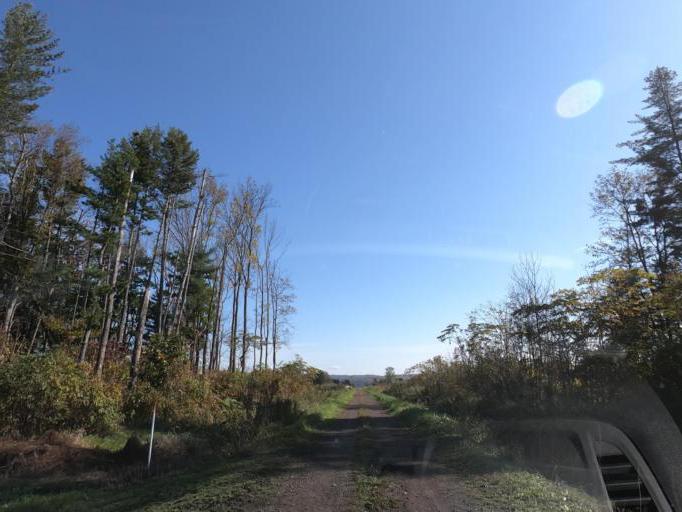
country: JP
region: Hokkaido
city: Obihiro
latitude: 42.9541
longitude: 143.2306
